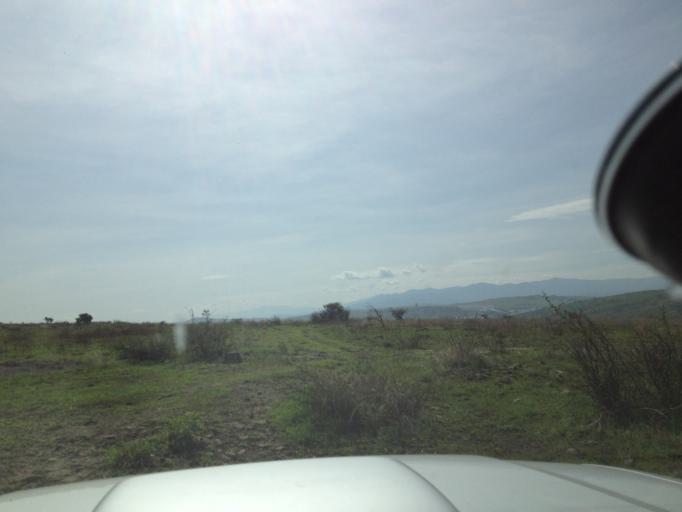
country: MX
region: Michoacan
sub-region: Tarimbaro
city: El Colegio
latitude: 19.7688
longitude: -101.1754
